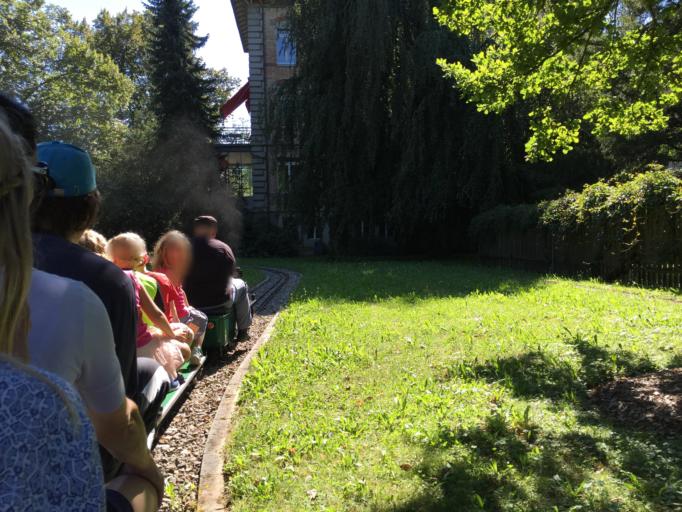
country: CH
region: Bern
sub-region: Bern-Mittelland District
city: Munsingen
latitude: 46.8812
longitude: 7.5544
